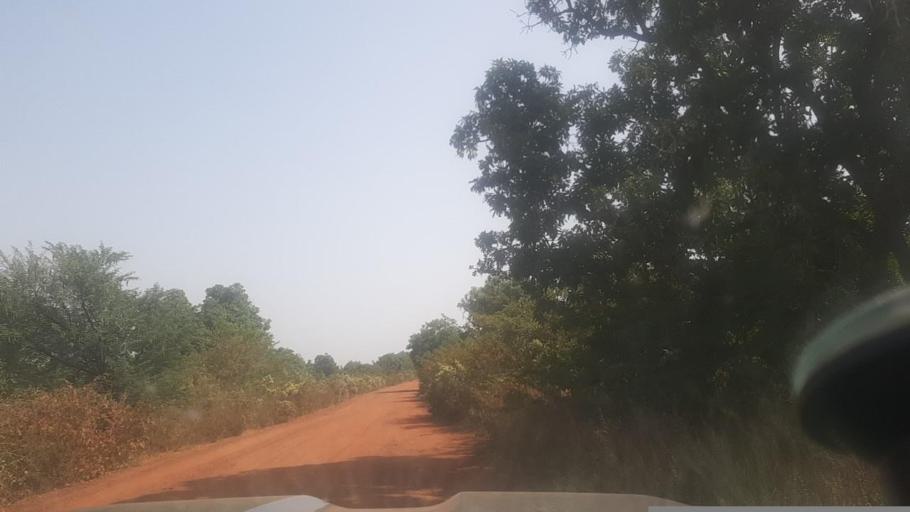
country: ML
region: Segou
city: Bla
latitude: 12.9222
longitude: -6.2625
